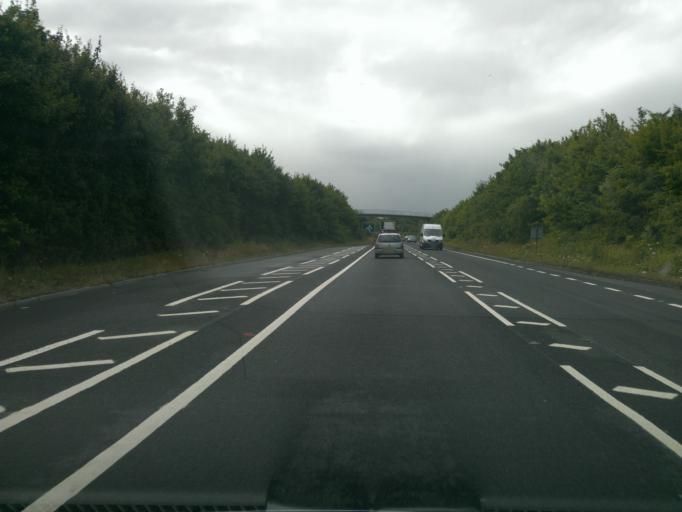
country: GB
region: England
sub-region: Essex
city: Little Clacton
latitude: 51.8231
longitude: 1.1342
